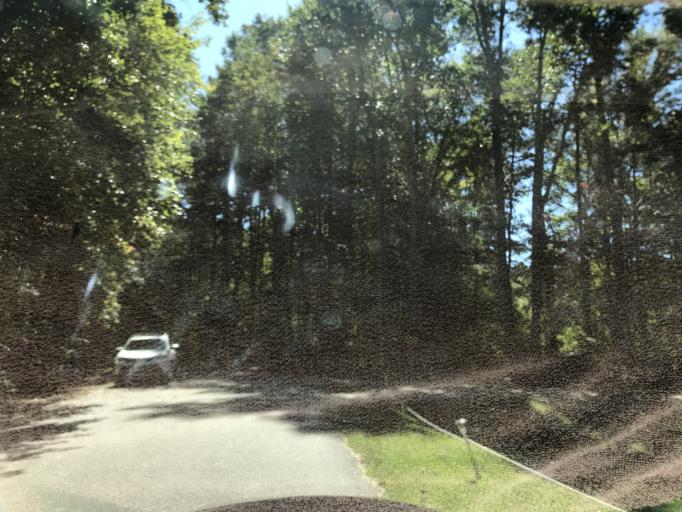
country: US
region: North Carolina
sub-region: Wake County
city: Wake Forest
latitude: 35.9453
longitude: -78.5903
